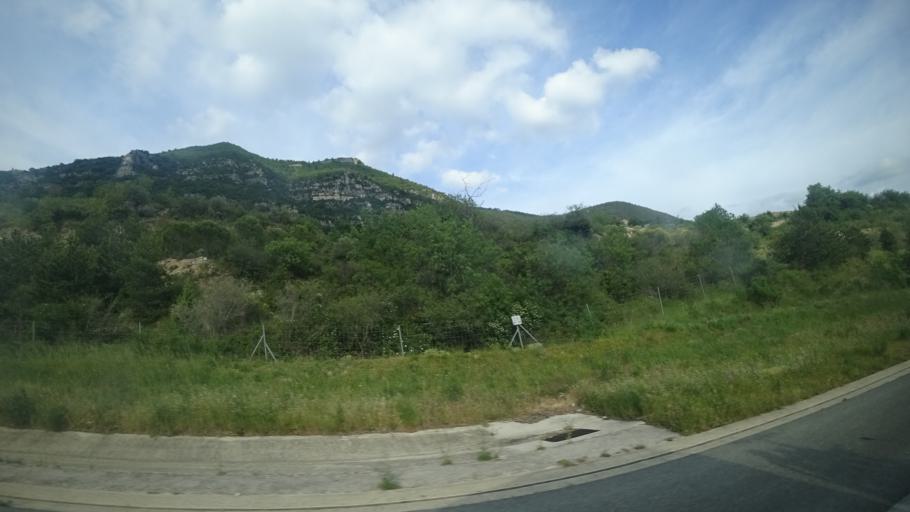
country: FR
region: Languedoc-Roussillon
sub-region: Departement de l'Herault
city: Lodeve
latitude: 43.7904
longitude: 3.3264
